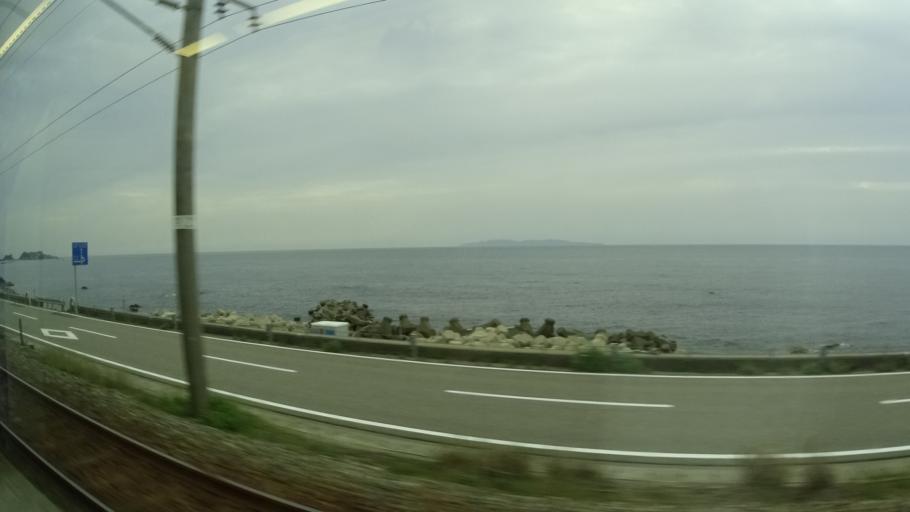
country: JP
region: Niigata
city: Murakami
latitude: 38.4608
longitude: 139.4986
